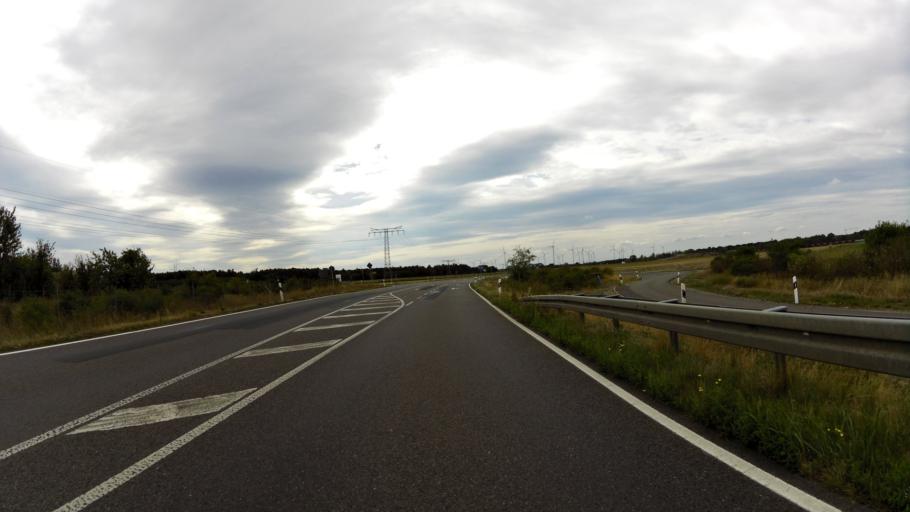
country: DE
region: Brandenburg
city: Heinersbruck
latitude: 51.8084
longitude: 14.5045
